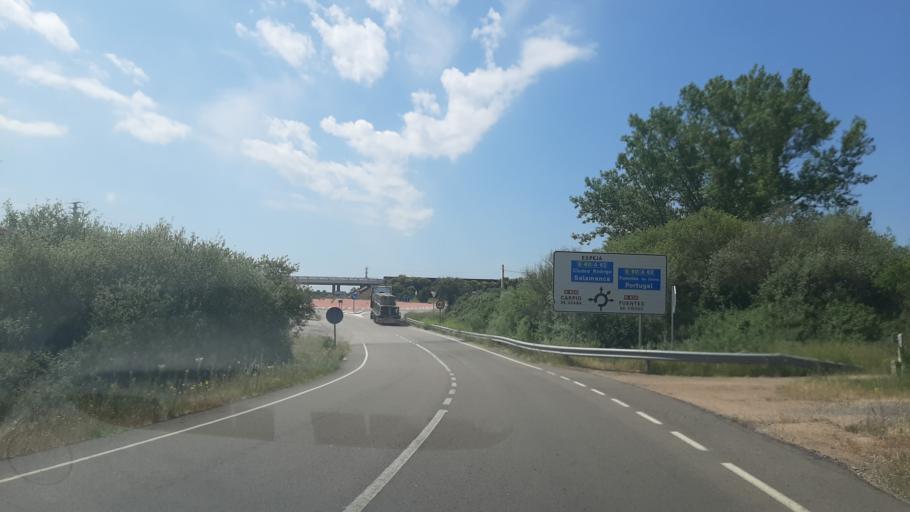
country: ES
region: Castille and Leon
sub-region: Provincia de Salamanca
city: Espeja
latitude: 40.5925
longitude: -6.7053
